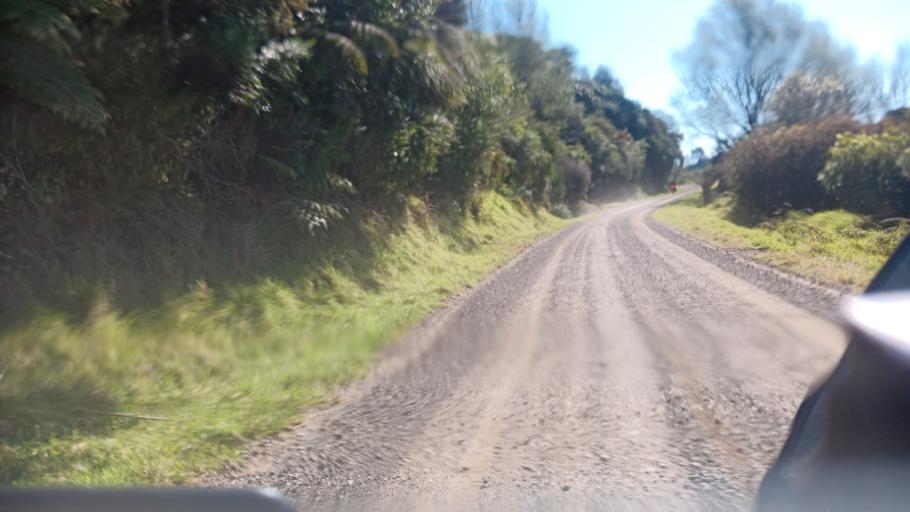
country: NZ
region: Bay of Plenty
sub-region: Opotiki District
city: Opotiki
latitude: -38.0177
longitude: 177.4300
